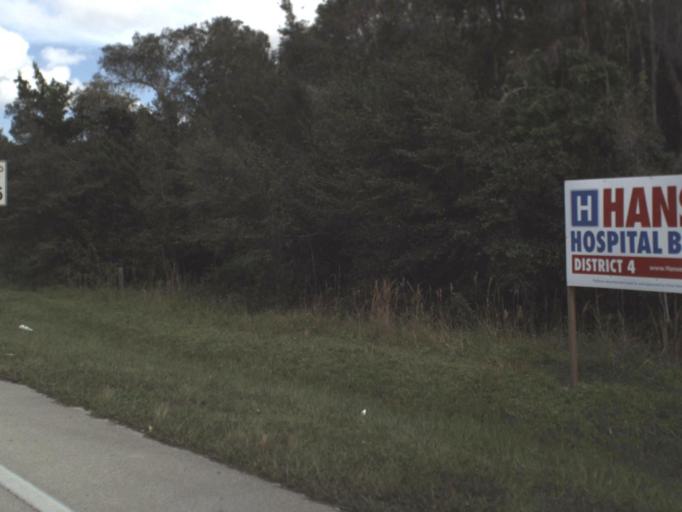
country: US
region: Florida
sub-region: Lee County
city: Pine Manor
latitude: 26.5862
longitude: -81.8533
